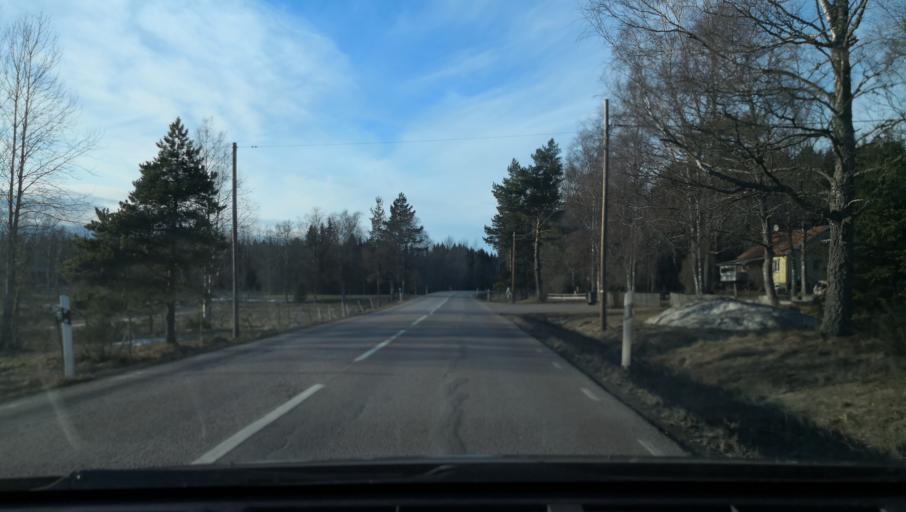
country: SE
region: Uppsala
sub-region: Osthammars Kommun
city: OEsthammar
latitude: 60.2991
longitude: 18.2804
